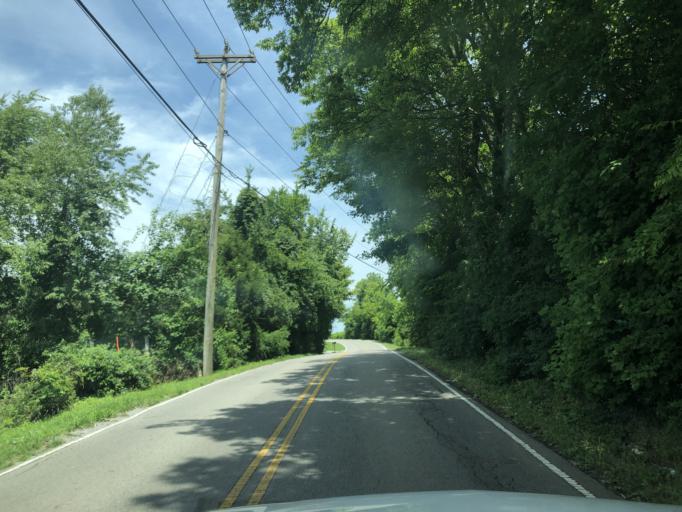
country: US
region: Tennessee
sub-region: Rutherford County
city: La Vergne
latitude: 36.0256
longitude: -86.6465
